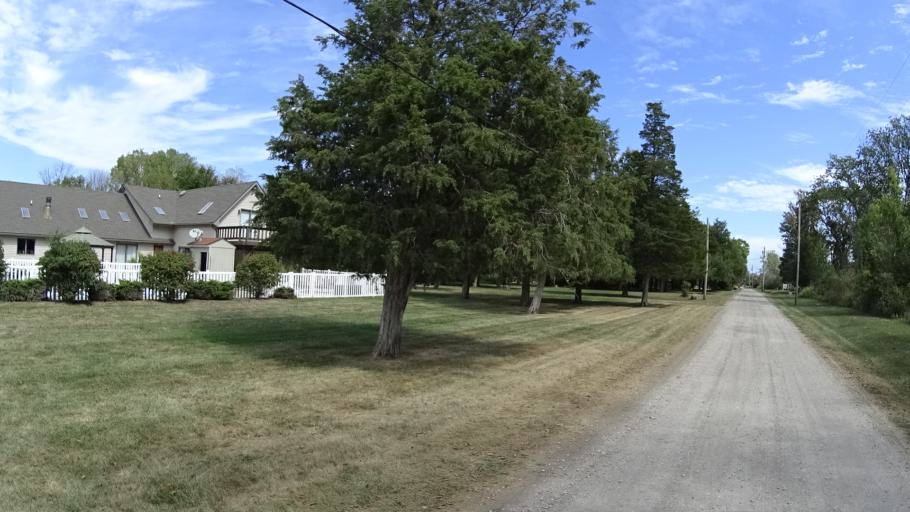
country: US
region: Ohio
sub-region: Erie County
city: Sandusky
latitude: 41.6011
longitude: -82.6866
